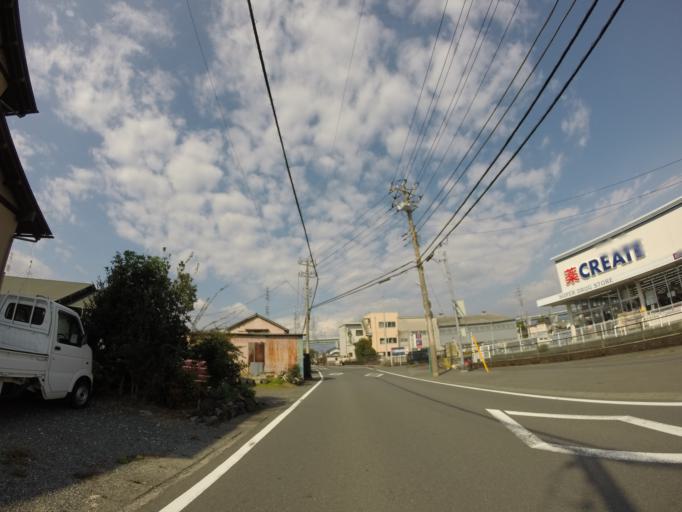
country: JP
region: Shizuoka
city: Fujinomiya
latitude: 35.1932
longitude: 138.6427
